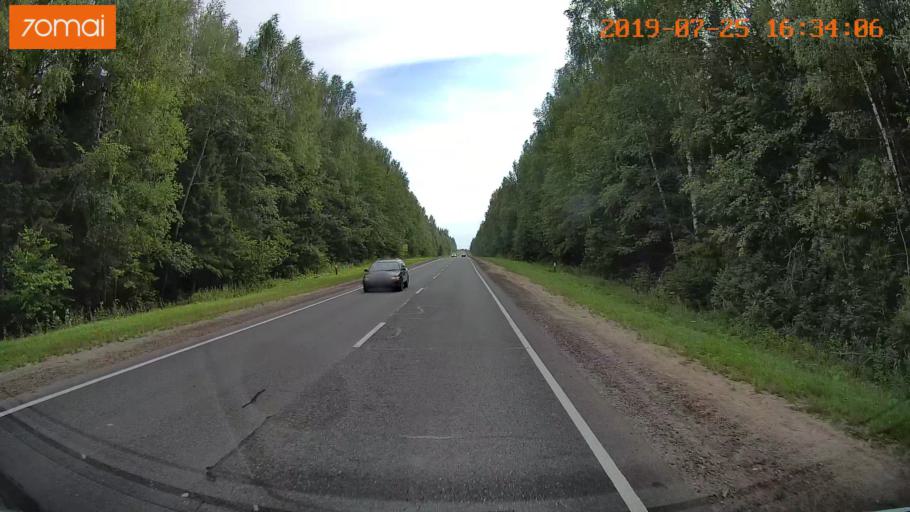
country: RU
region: Ivanovo
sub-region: Privolzhskiy Rayon
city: Ples
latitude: 57.4201
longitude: 41.4435
